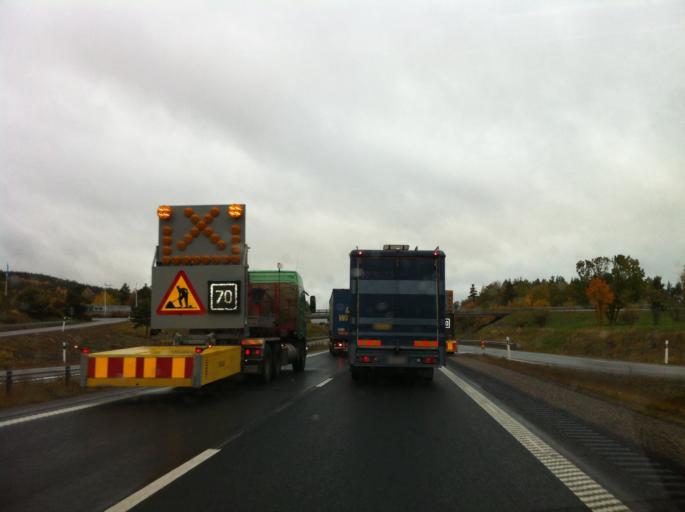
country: SE
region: Joenkoeping
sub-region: Jonkopings Kommun
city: Kaxholmen
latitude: 57.9259
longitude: 14.3193
